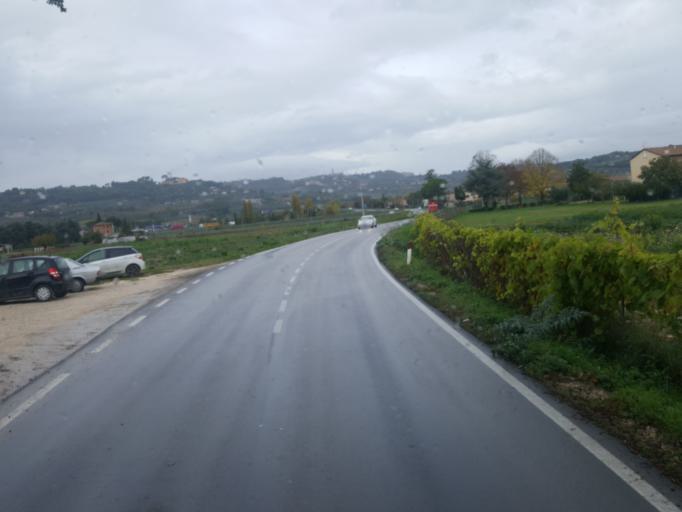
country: IT
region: Umbria
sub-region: Provincia di Perugia
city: San Martino in Campo
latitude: 43.0726
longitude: 12.4258
